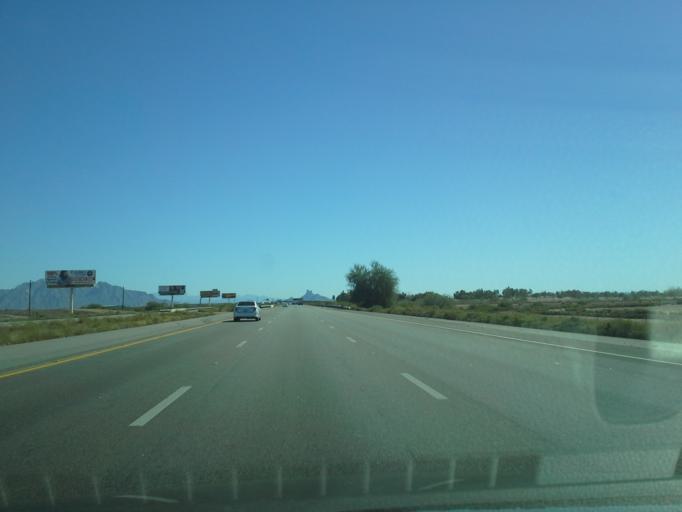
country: US
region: Arizona
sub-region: Pinal County
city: Eloy
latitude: 32.7727
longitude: -111.6121
